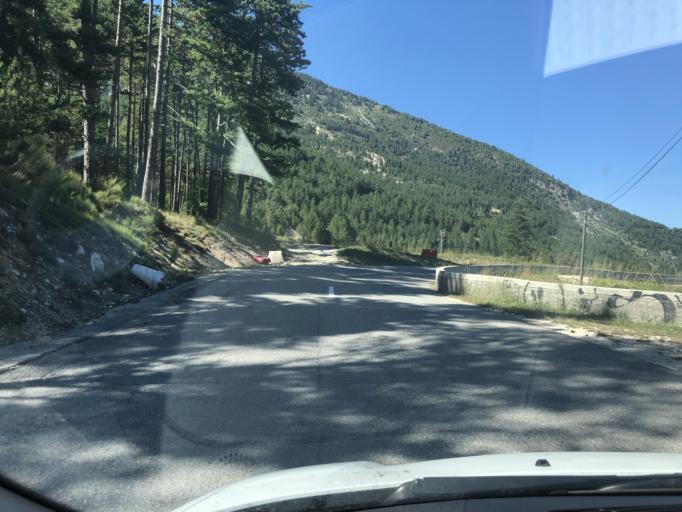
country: FR
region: Provence-Alpes-Cote d'Azur
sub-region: Departement des Alpes-de-Haute-Provence
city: Annot
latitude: 43.9955
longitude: 6.5390
